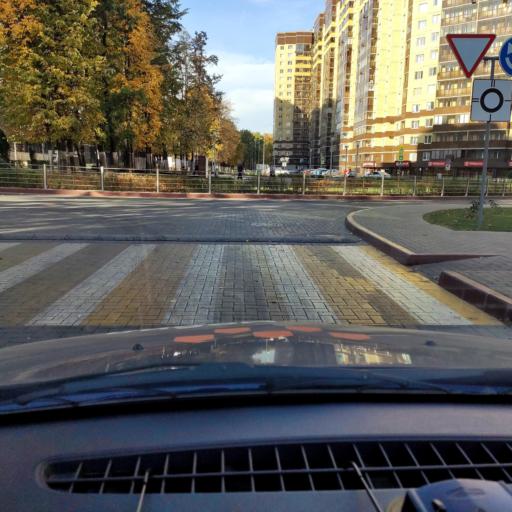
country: RU
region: Voronezj
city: Voronezh
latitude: 51.7147
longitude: 39.1963
